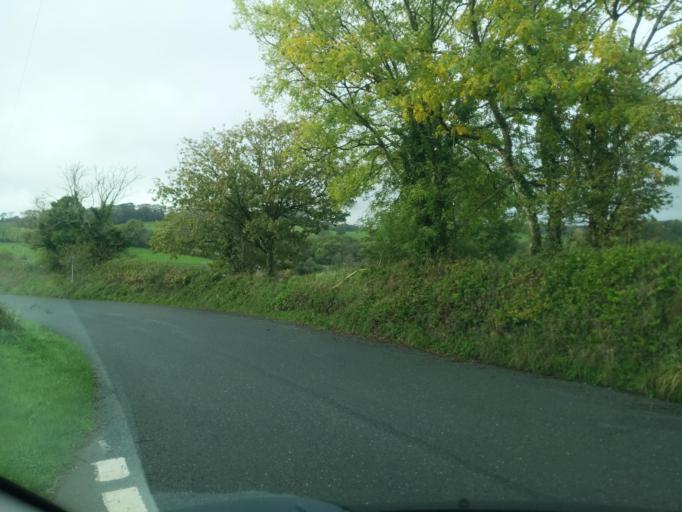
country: GB
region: England
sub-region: Cornwall
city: Saltash
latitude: 50.4532
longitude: -4.2460
